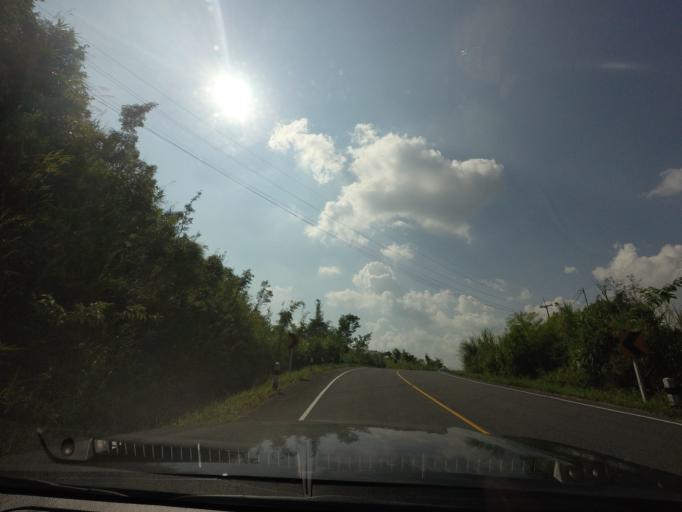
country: TH
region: Nan
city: Santi Suk
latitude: 18.9752
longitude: 101.0127
